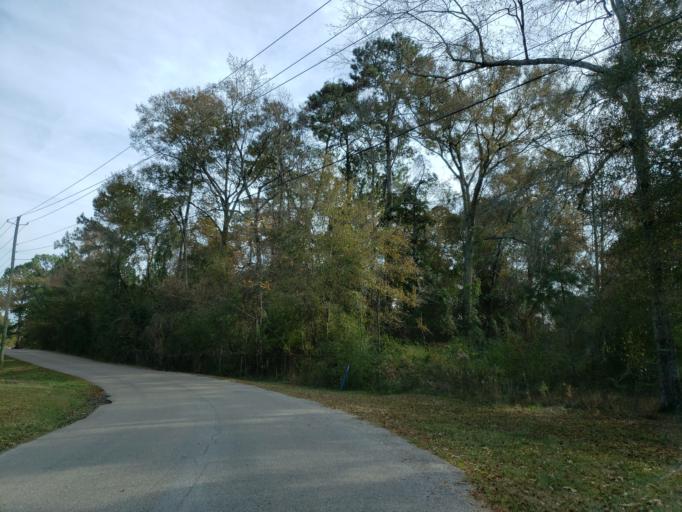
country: US
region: Mississippi
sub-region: Forrest County
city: Glendale
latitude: 31.3497
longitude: -89.3205
